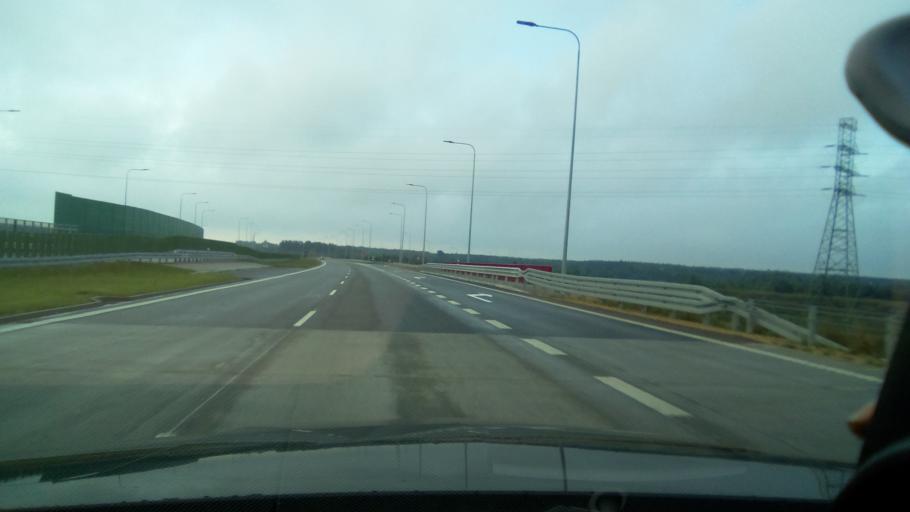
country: PL
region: Silesian Voivodeship
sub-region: Powiat czestochowski
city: Blachownia
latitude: 50.7818
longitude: 19.0034
